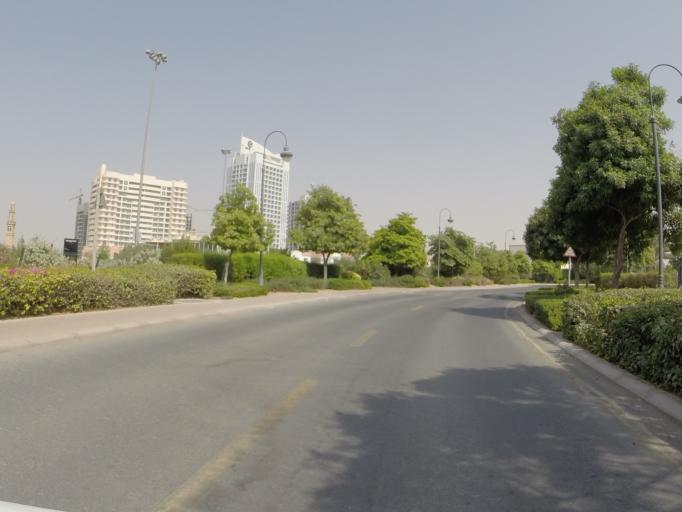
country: AE
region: Dubai
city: Dubai
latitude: 25.0316
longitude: 55.2195
